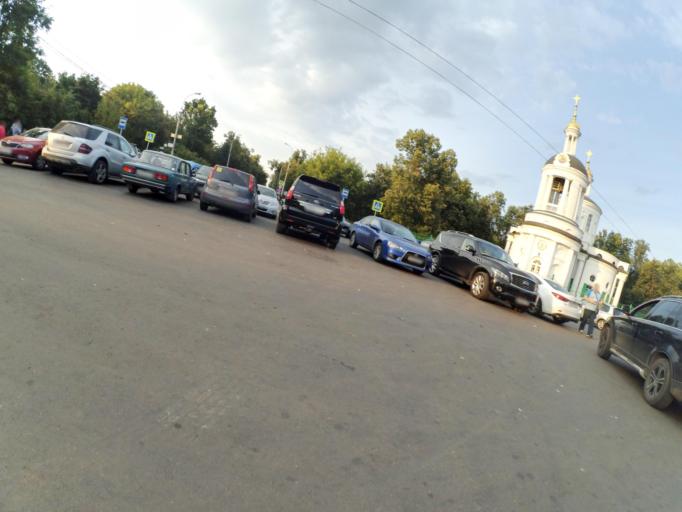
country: RU
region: Moscow
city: Kuz'minki
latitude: 55.6904
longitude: 37.7894
